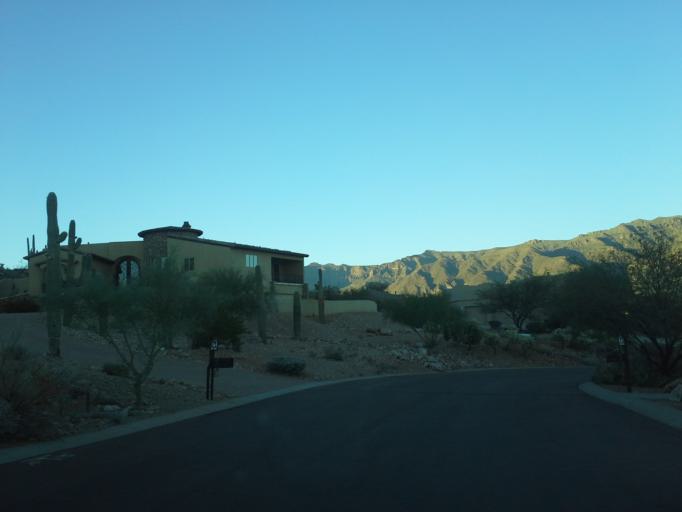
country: US
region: Arizona
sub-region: Pinal County
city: Apache Junction
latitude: 33.3680
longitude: -111.4400
